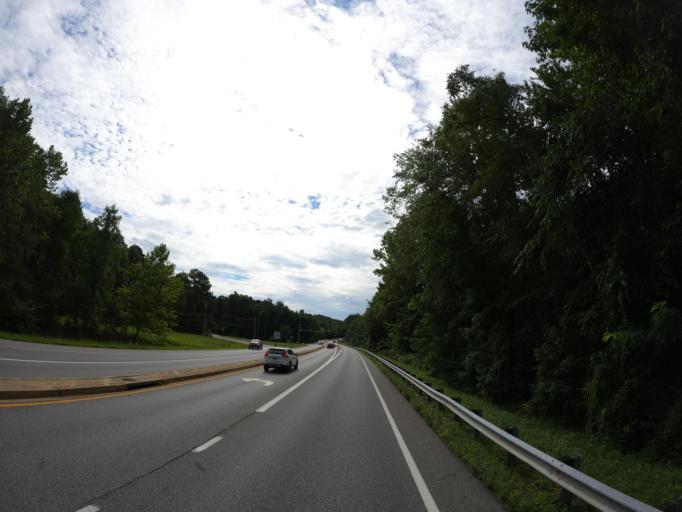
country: US
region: Maryland
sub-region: Saint Mary's County
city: Leonardtown
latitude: 38.2861
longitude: -76.6208
